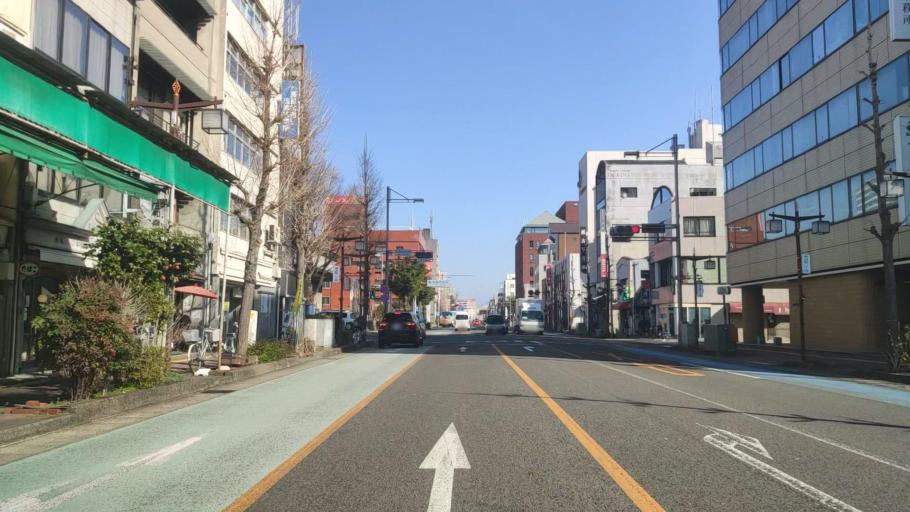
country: JP
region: Gifu
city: Gifu-shi
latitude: 35.4223
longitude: 136.7610
